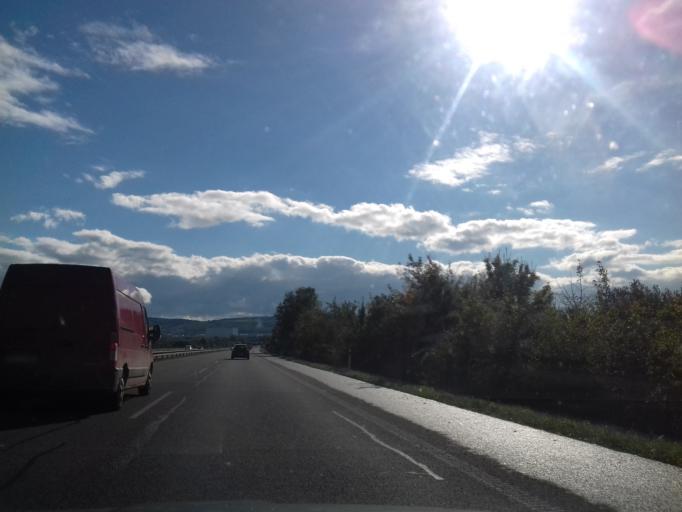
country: CZ
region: Central Bohemia
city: Kosmonosy
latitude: 50.4387
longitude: 14.9427
